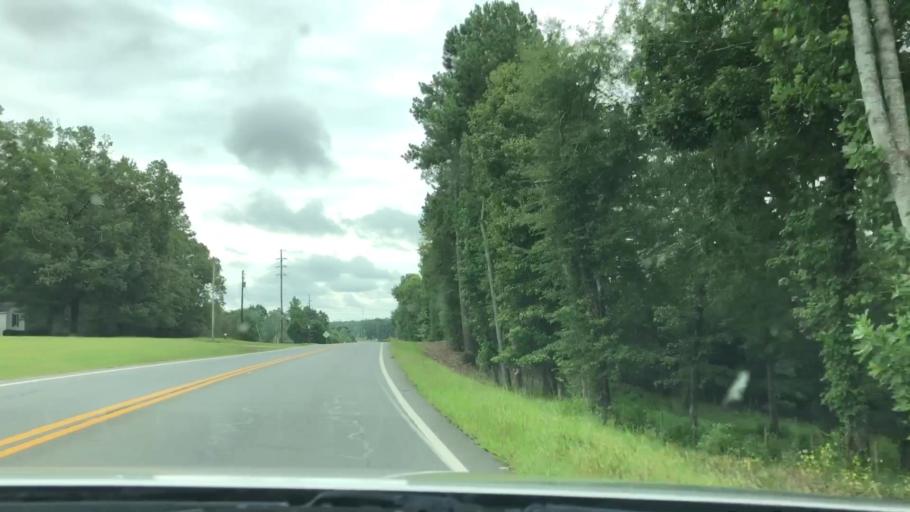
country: US
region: Georgia
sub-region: Pike County
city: Zebulon
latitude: 33.1075
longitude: -84.3661
